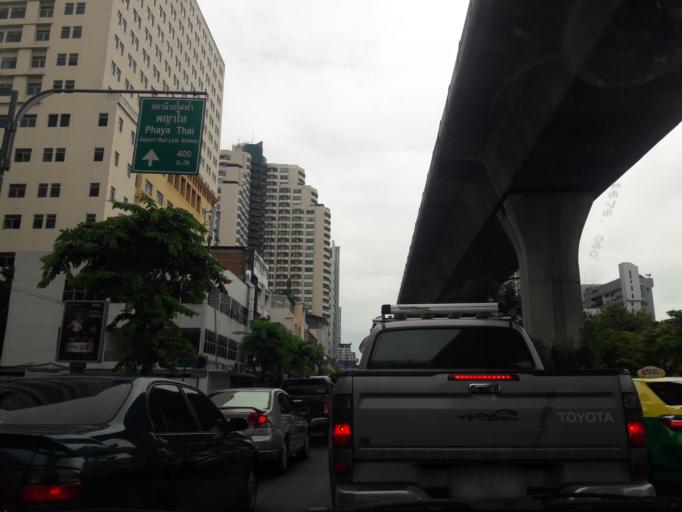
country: TH
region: Bangkok
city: Ratchathewi
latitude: 13.7607
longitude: 100.5360
